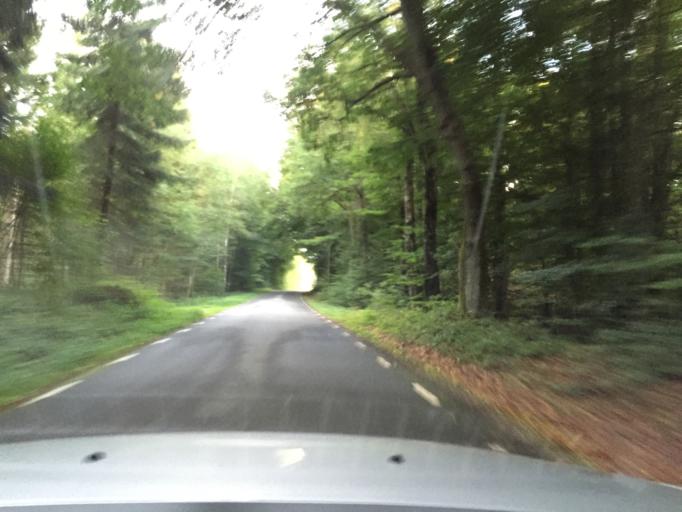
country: SE
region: Skane
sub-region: Hassleholms Kommun
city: Vinslov
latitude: 56.0254
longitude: 13.8217
